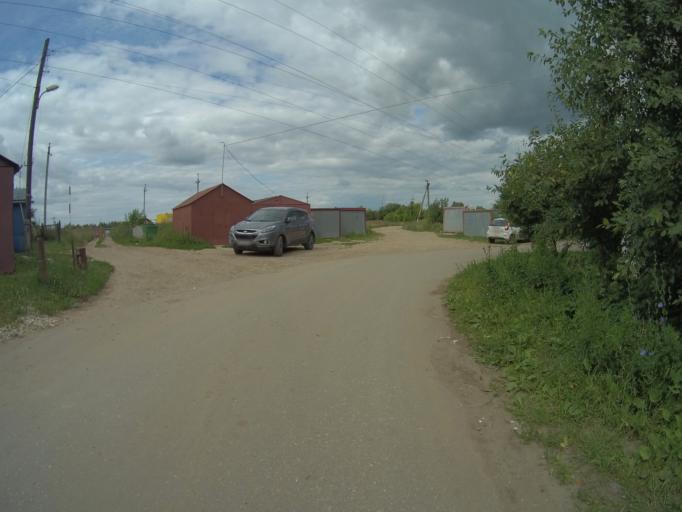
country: RU
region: Vladimir
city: Bogolyubovo
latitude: 56.2008
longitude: 40.5287
